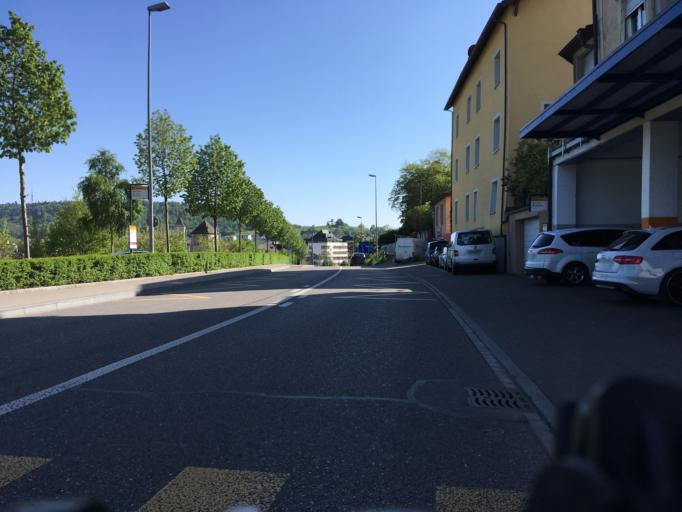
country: CH
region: Schaffhausen
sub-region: Bezirk Schaffhausen
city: Schaffhausen
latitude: 47.7025
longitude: 8.6350
